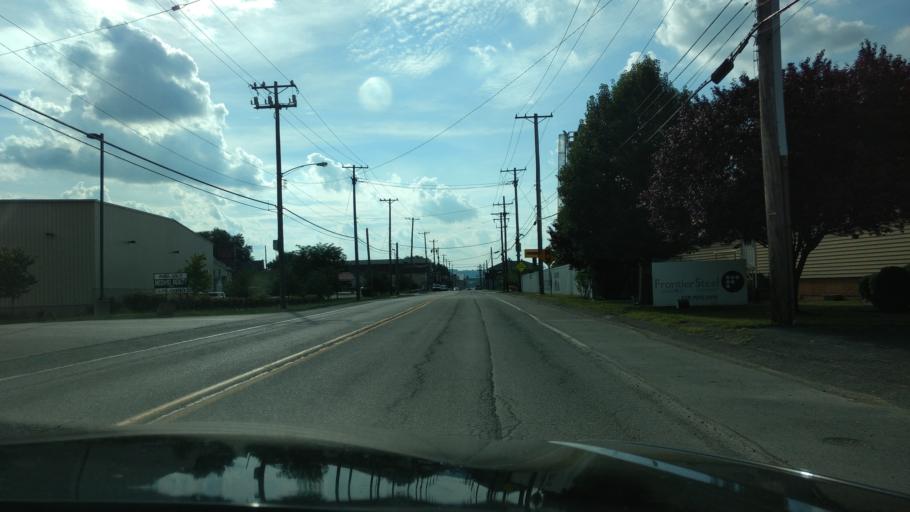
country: US
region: Pennsylvania
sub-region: Allegheny County
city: Emsworth
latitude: 40.5096
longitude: -80.1228
